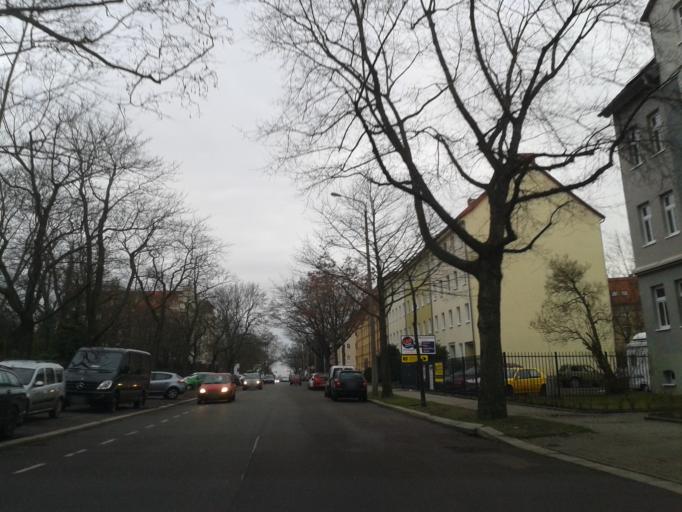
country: DE
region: Saxony-Anhalt
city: Halle (Saale)
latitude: 51.4630
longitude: 11.9763
